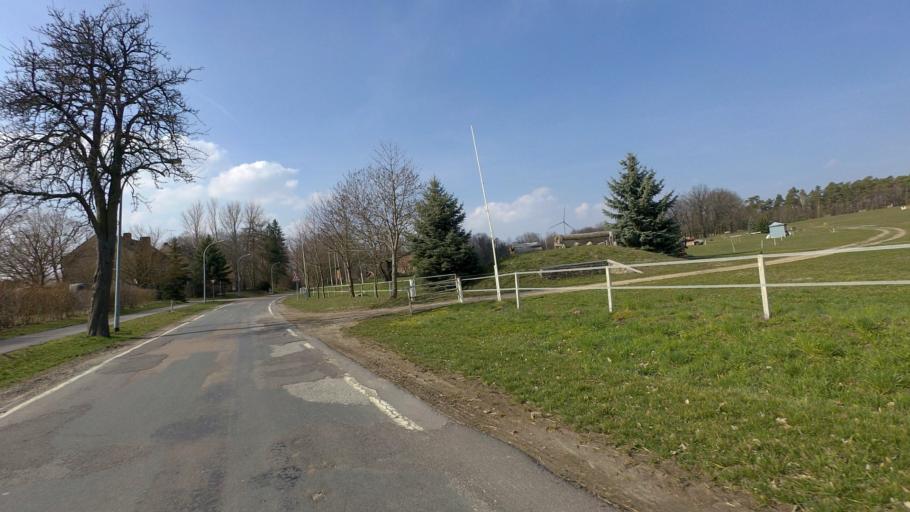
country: DE
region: Brandenburg
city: Ihlow
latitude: 51.9512
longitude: 13.3680
